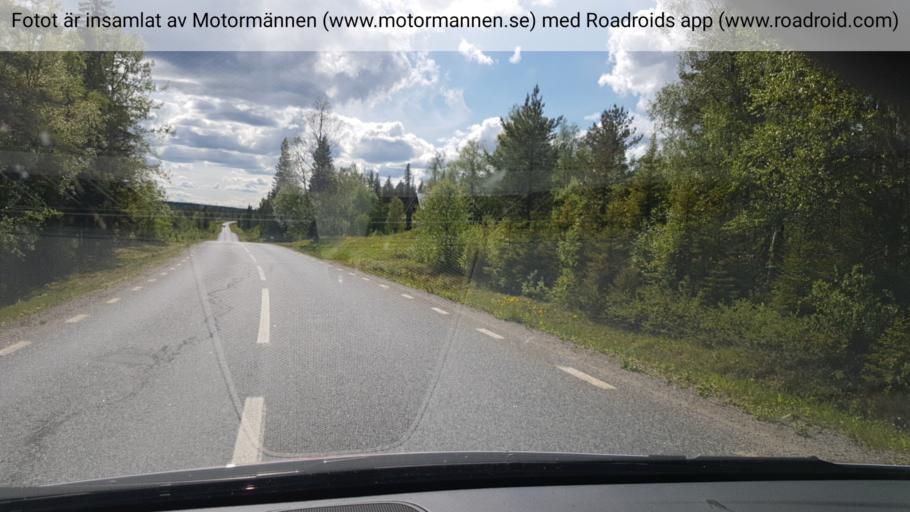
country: SE
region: Vaesterbotten
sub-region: Skelleftea Kommun
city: Burtraesk
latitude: 64.3932
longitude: 20.2947
